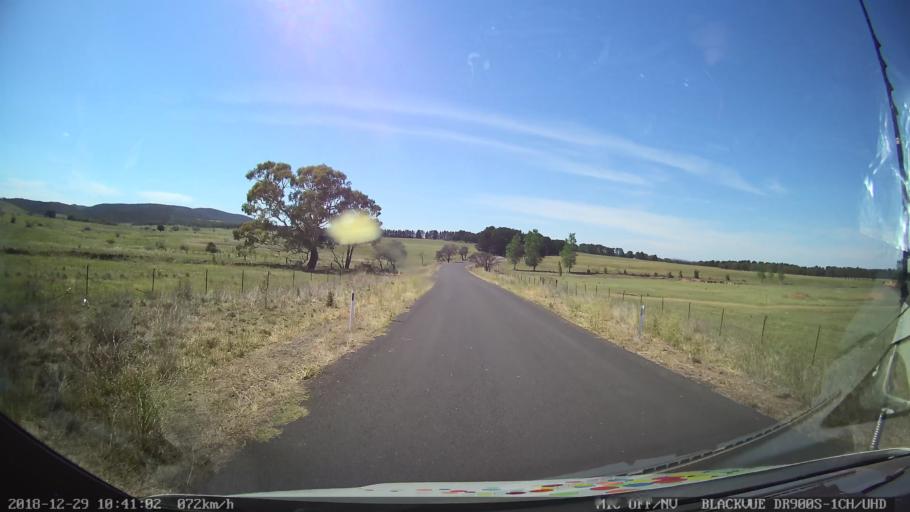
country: AU
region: New South Wales
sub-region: Palerang
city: Bungendore
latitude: -35.0210
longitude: 149.5198
